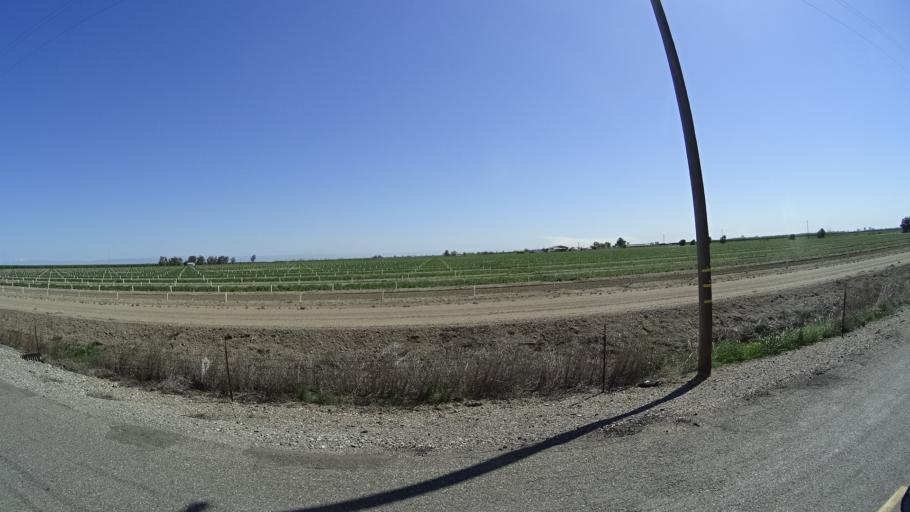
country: US
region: California
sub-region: Glenn County
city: Willows
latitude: 39.6338
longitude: -122.2535
